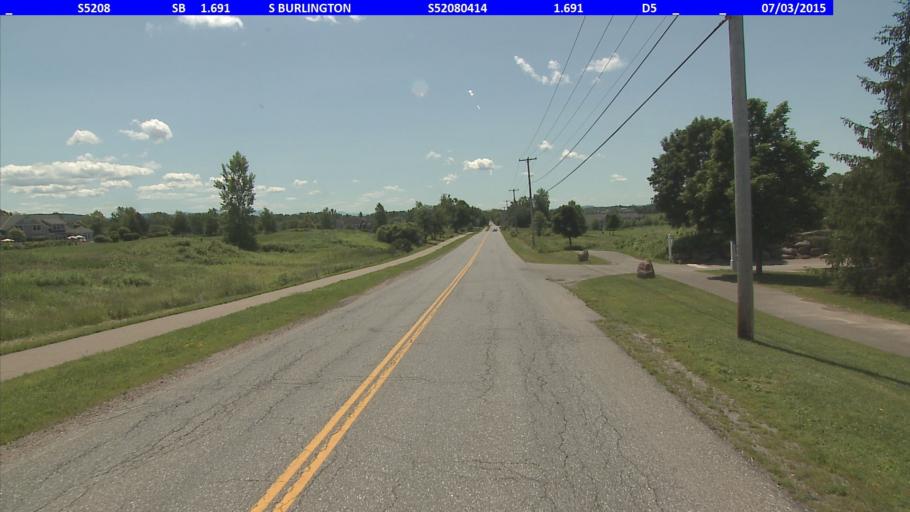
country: US
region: Vermont
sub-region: Chittenden County
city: South Burlington
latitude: 44.4350
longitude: -73.1758
